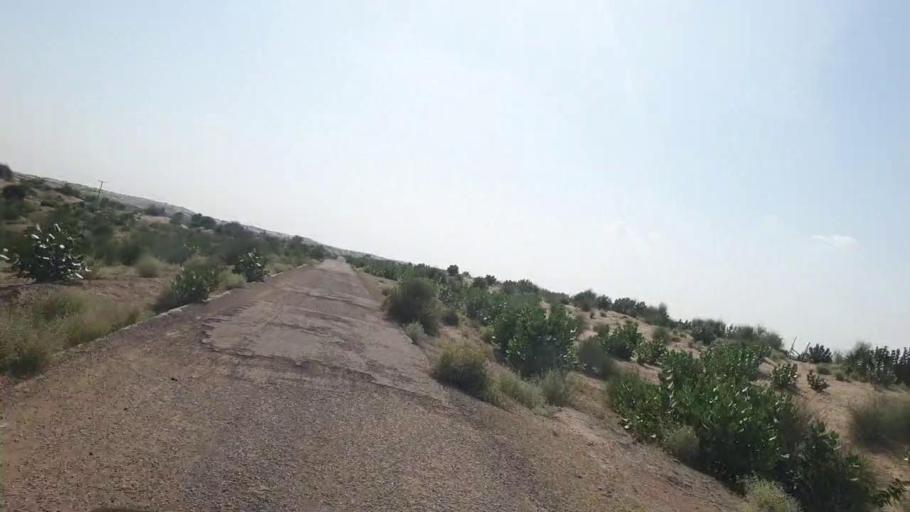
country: PK
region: Sindh
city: Chor
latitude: 25.5573
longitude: 70.2214
